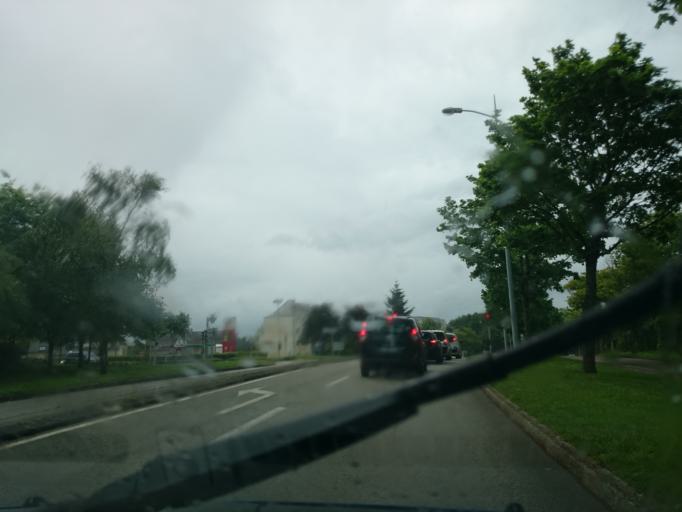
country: FR
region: Brittany
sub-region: Departement du Morbihan
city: Vannes
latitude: 47.6419
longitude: -2.7750
